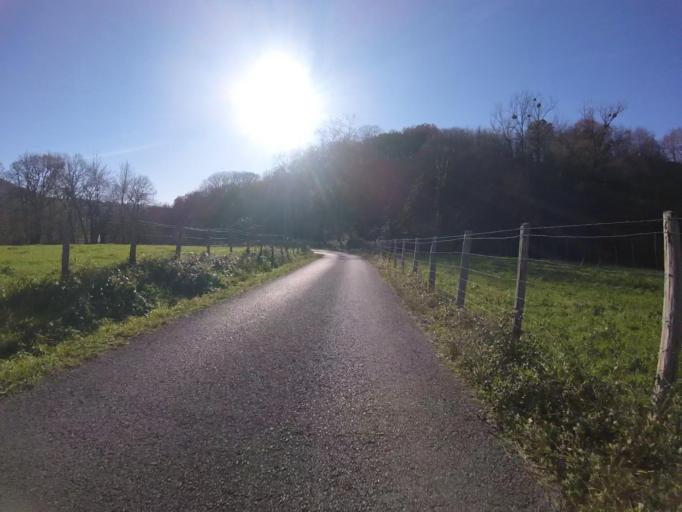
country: ES
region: Navarre
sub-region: Provincia de Navarra
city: Bera
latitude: 43.2917
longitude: -1.6482
